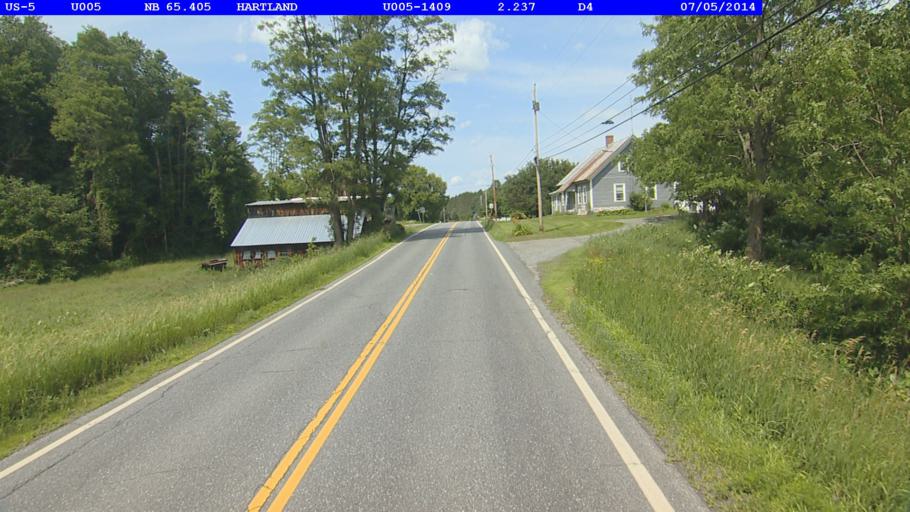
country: US
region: Vermont
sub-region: Windsor County
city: Windsor
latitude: 43.5444
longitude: -72.3883
